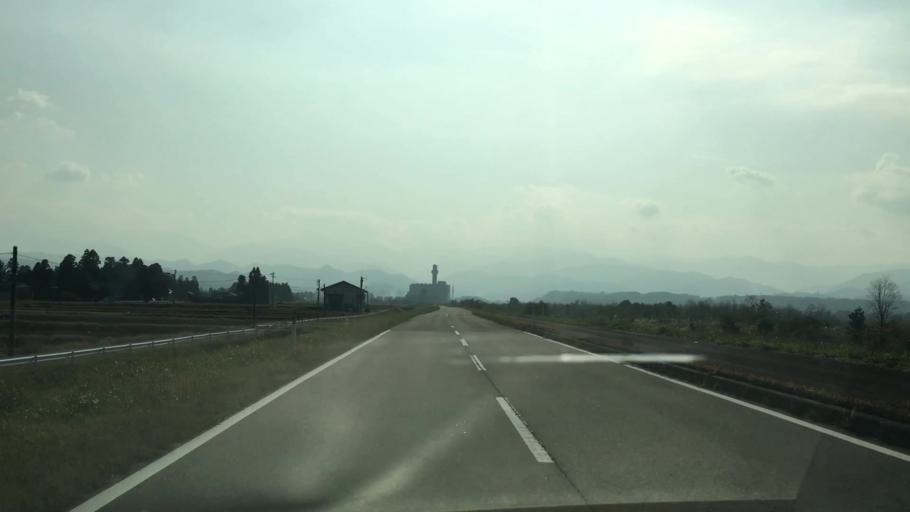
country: JP
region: Toyama
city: Toyama-shi
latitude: 36.6382
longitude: 137.2902
